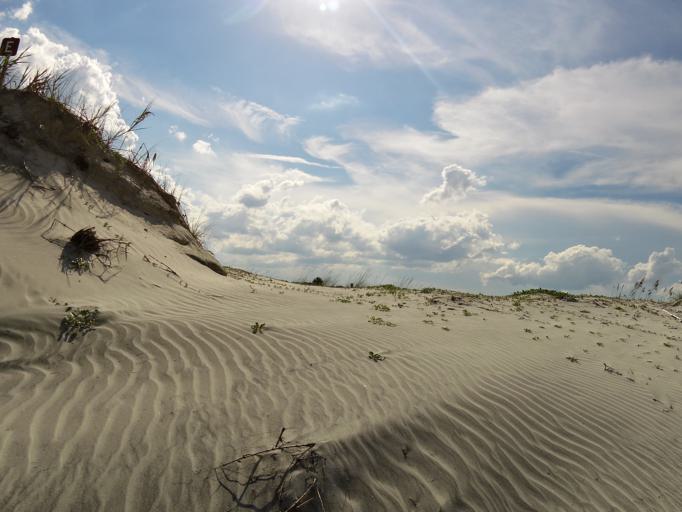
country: US
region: Florida
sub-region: Duval County
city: Atlantic Beach
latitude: 30.4541
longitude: -81.4109
